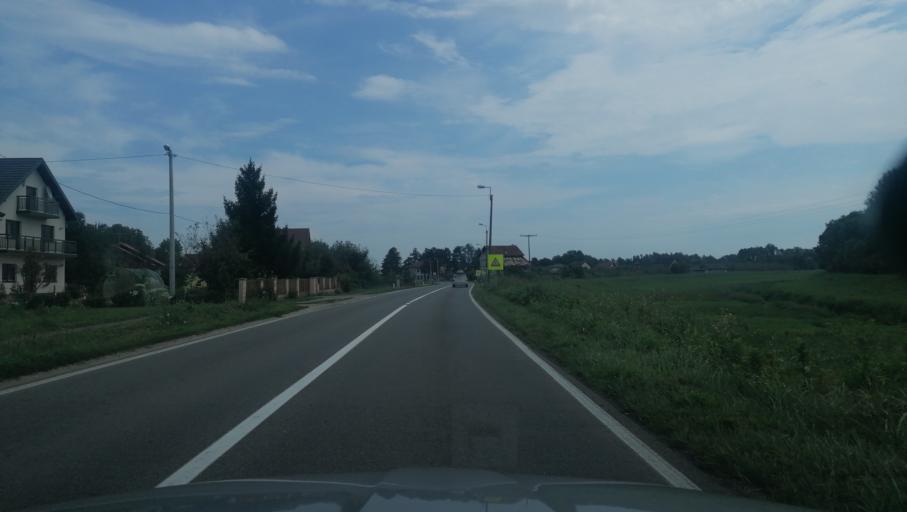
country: BA
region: Brcko
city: Brka
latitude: 44.9286
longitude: 18.7131
